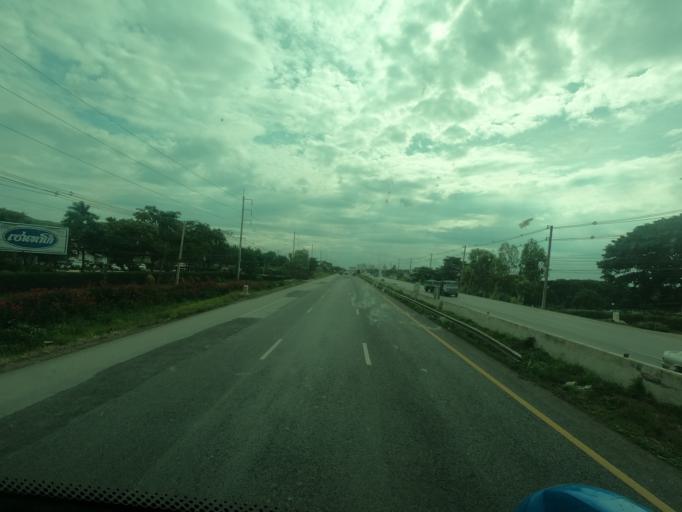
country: TH
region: Nakhon Ratchasima
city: Pak Chong
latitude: 14.6565
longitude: 101.3251
